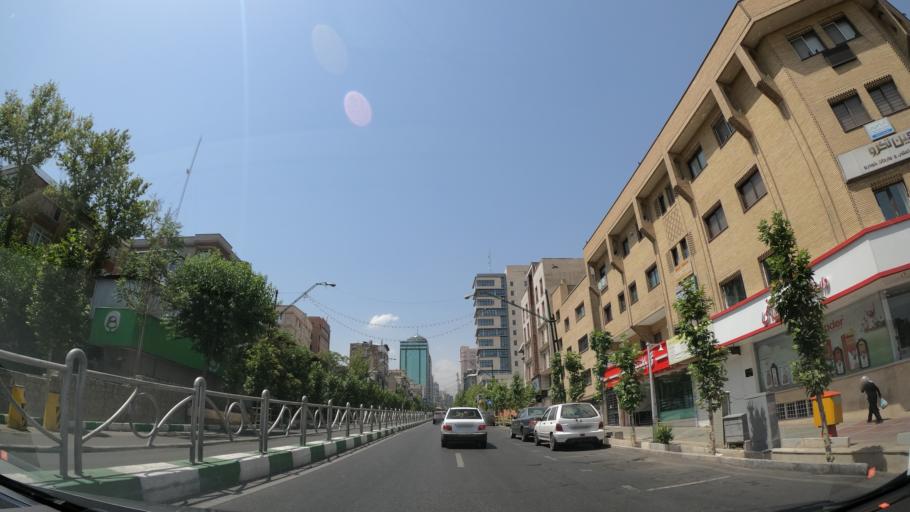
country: IR
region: Tehran
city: Tehran
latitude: 35.7290
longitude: 51.4128
